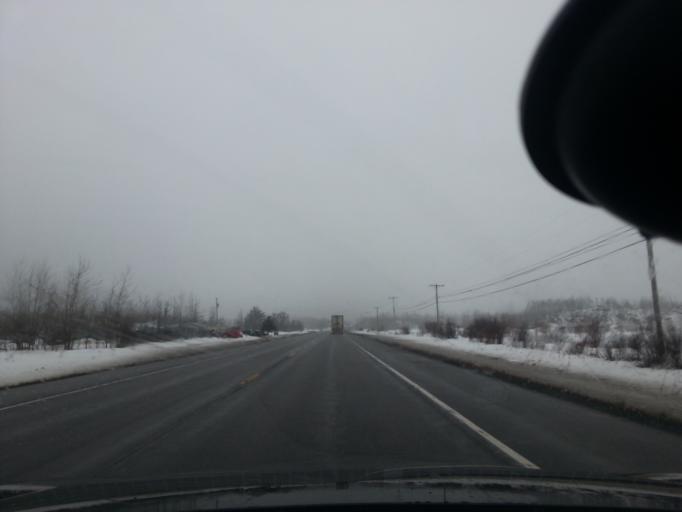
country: US
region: New York
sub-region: Jefferson County
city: Philadelphia
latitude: 44.1674
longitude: -75.6805
